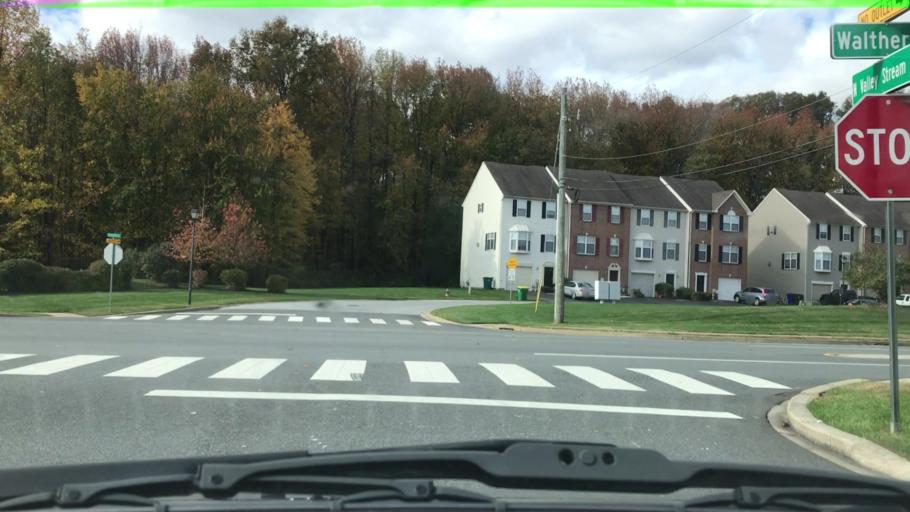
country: US
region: Delaware
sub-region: New Castle County
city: Bear
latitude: 39.6495
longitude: -75.6876
